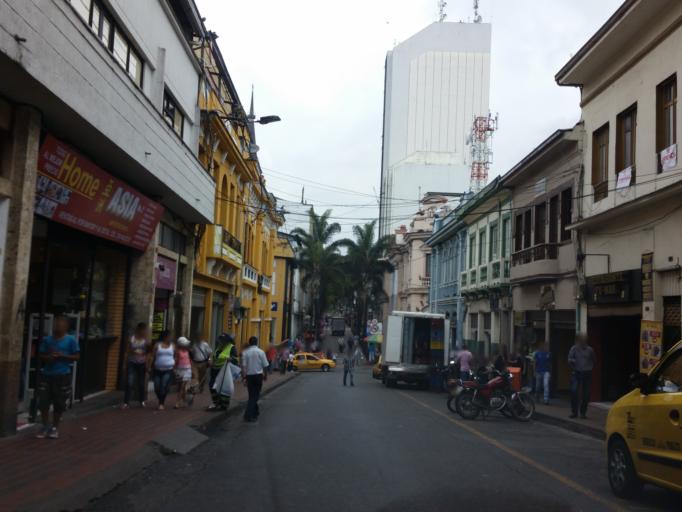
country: CO
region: Caldas
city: Manizales
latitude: 5.0670
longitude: -75.5200
